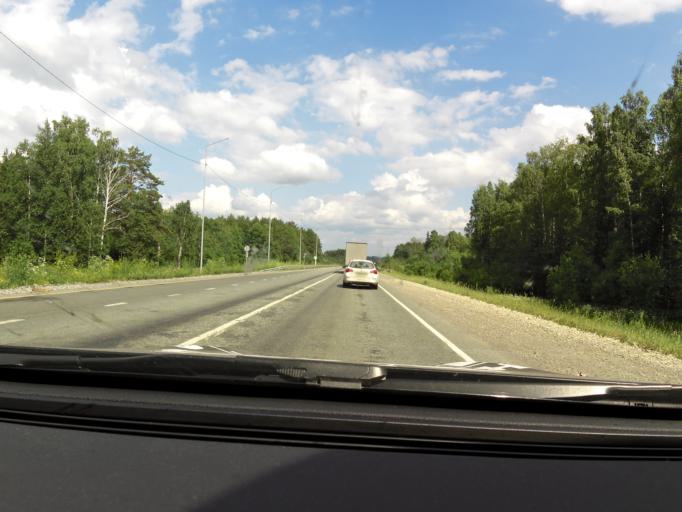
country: RU
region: Sverdlovsk
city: Bisert'
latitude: 56.8290
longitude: 59.0181
